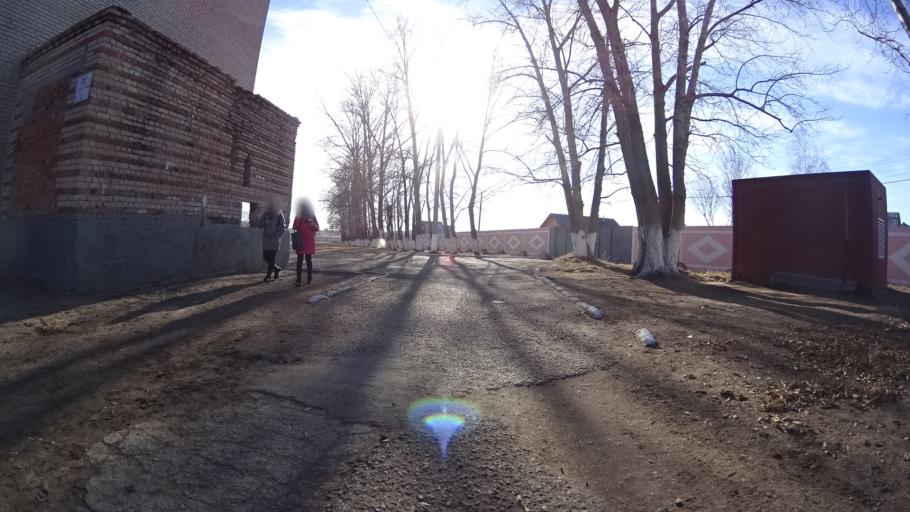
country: RU
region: Chelyabinsk
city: Troitsk
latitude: 54.0908
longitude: 61.5882
